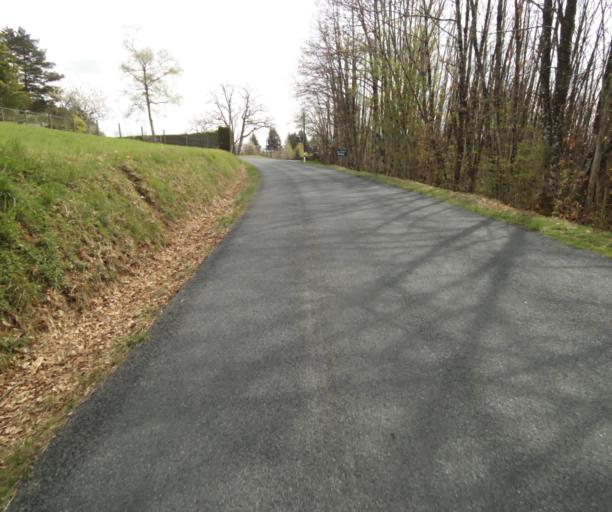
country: FR
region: Limousin
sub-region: Departement de la Correze
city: Sainte-Fortunade
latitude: 45.1983
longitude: 1.8364
